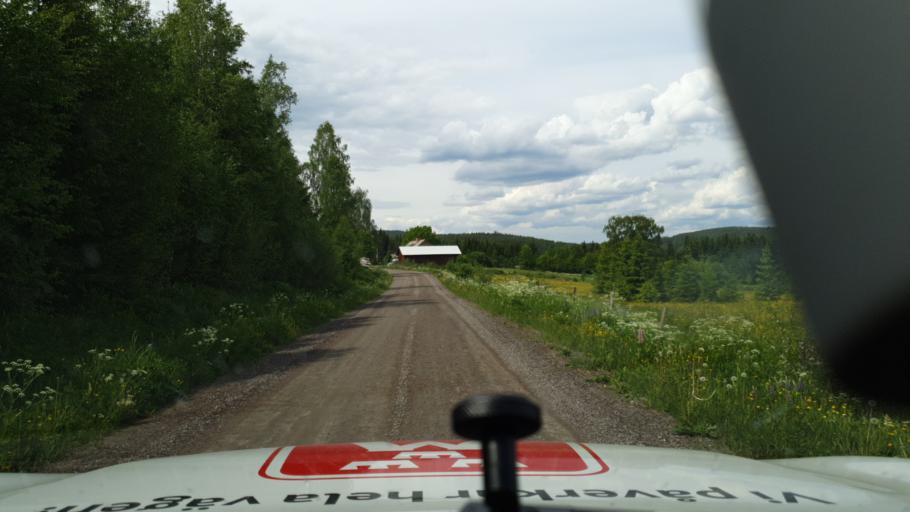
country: SE
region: Vaermland
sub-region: Torsby Kommun
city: Torsby
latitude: 59.9766
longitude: 12.8510
